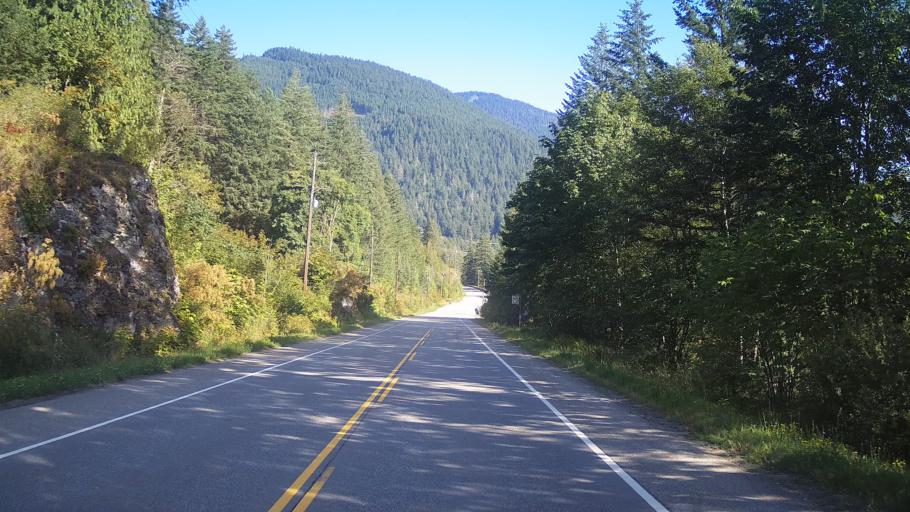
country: CA
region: British Columbia
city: Hope
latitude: 49.5450
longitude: -121.4393
